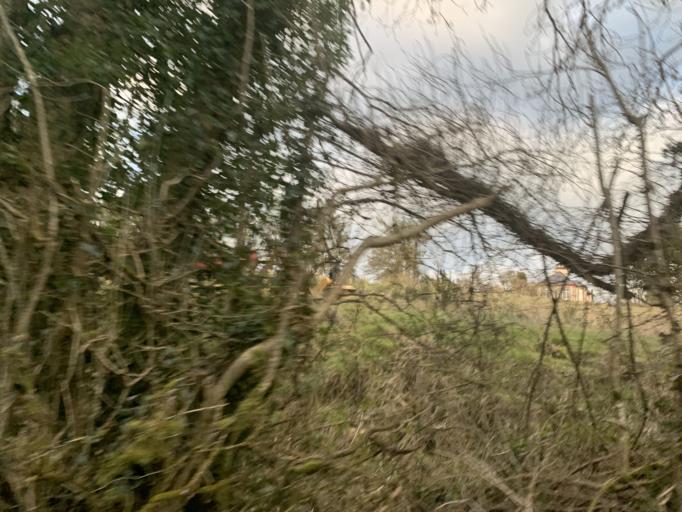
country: IE
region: Connaught
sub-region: Maigh Eo
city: Ballyhaunis
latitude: 53.8359
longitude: -8.7119
